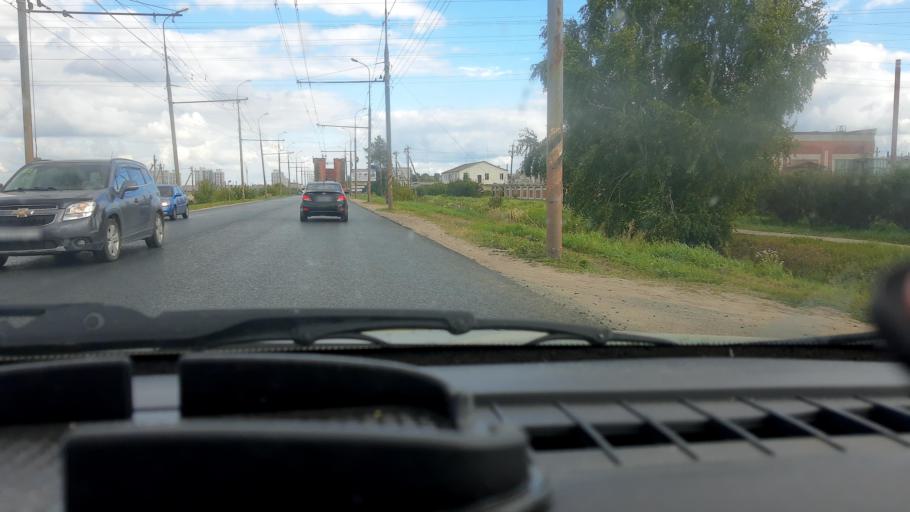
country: RU
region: Mariy-El
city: Medvedevo
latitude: 56.6383
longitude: 47.7796
